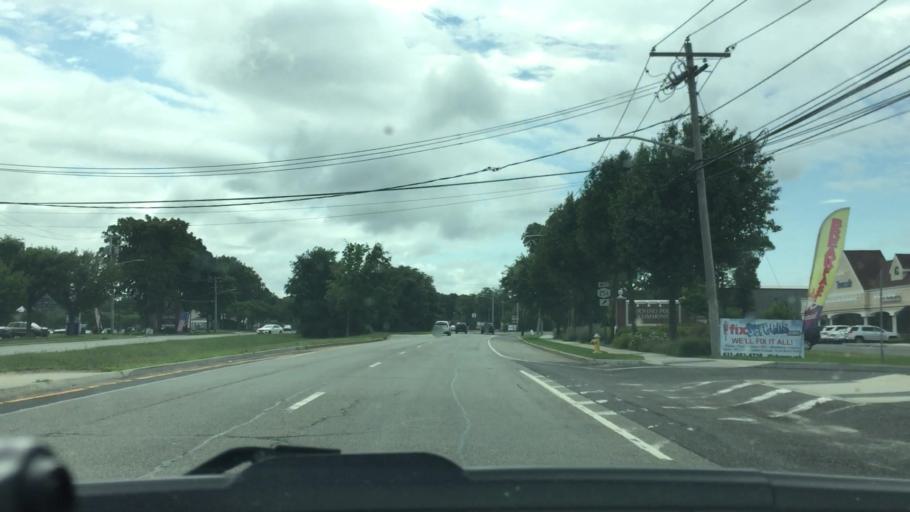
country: US
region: New York
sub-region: Suffolk County
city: Mount Sinai
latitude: 40.9330
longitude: -73.0298
